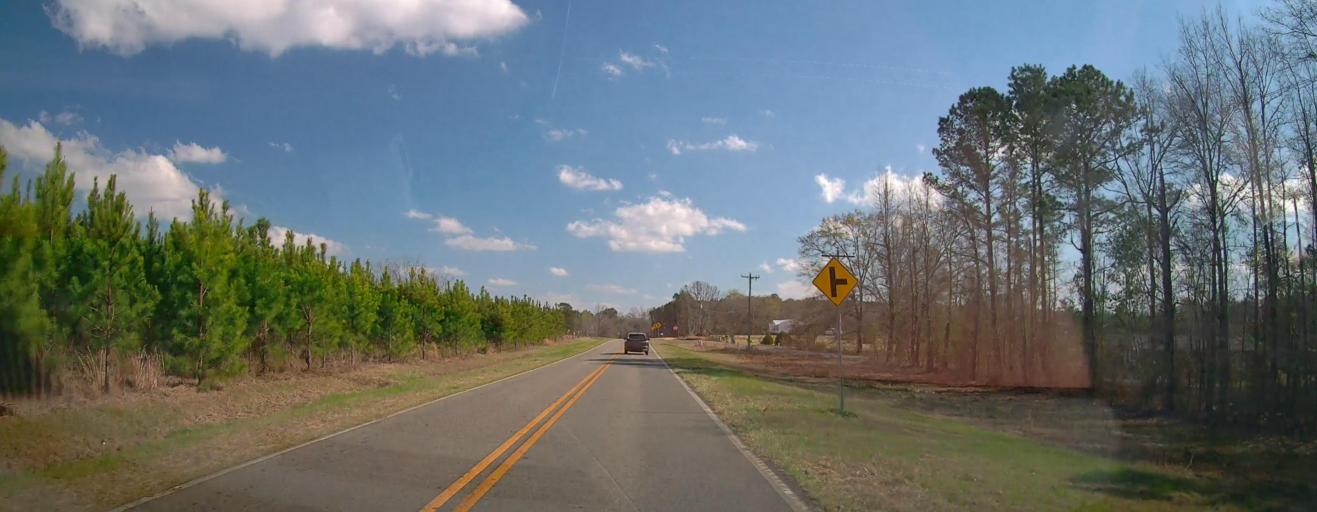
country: US
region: Georgia
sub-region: Laurens County
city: Dublin
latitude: 32.5995
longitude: -83.0726
